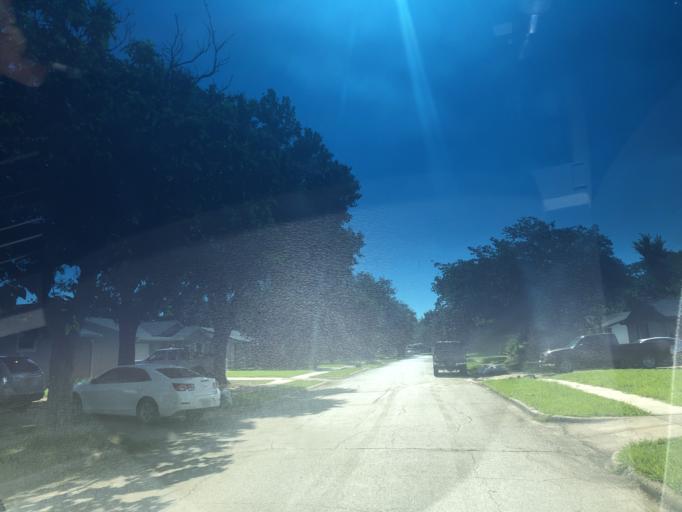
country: US
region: Texas
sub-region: Dallas County
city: Grand Prairie
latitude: 32.7147
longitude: -97.0111
